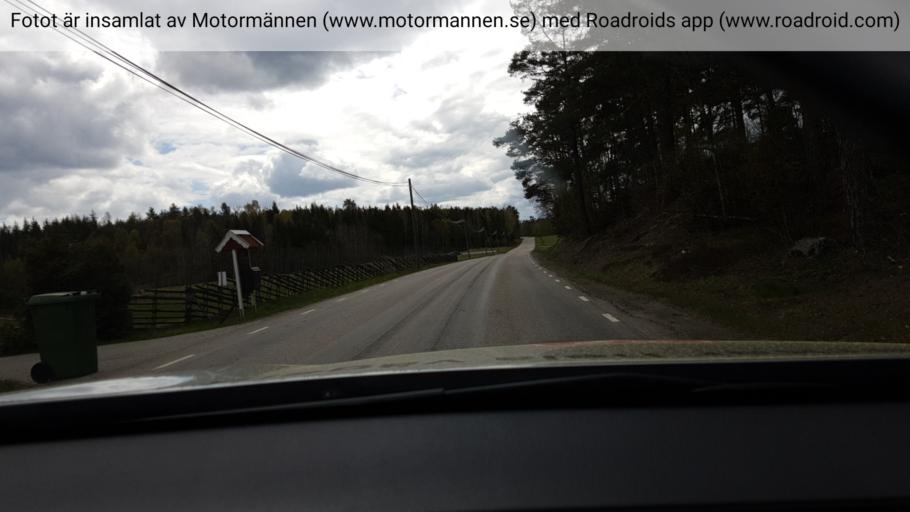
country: SE
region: Stockholm
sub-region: Haninge Kommun
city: Haninge
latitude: 59.0995
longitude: 18.1839
